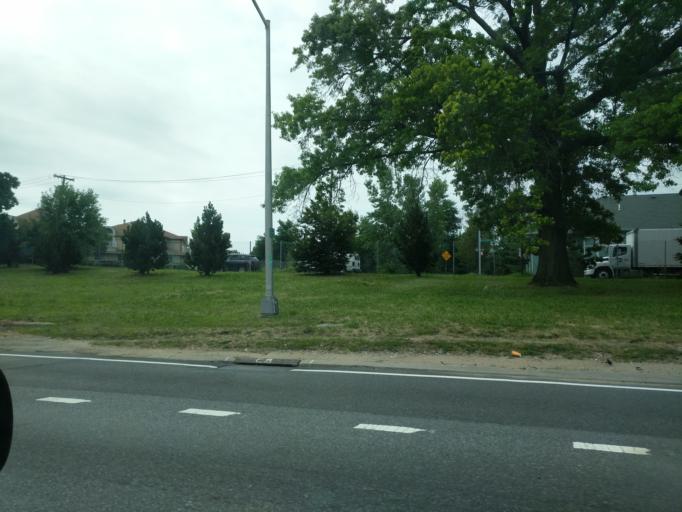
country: US
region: New York
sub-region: Queens County
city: Jamaica
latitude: 40.6674
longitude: -73.7720
